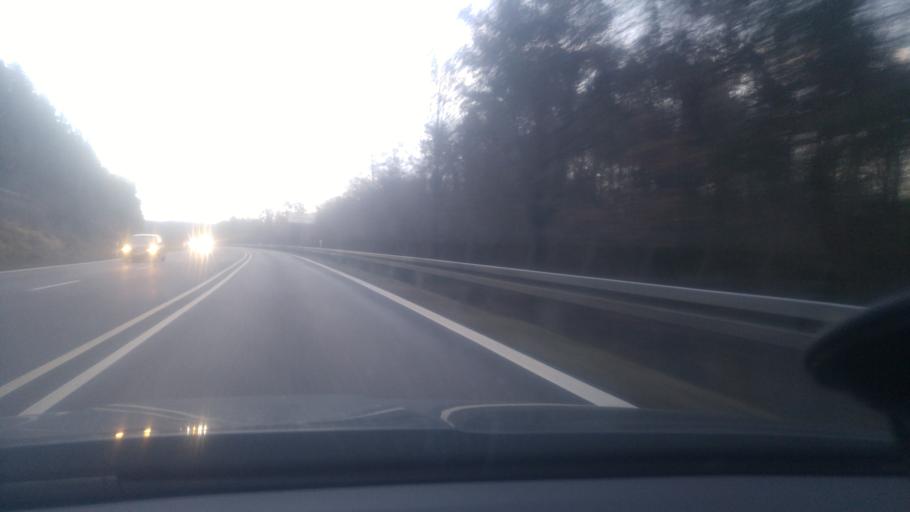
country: DE
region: Baden-Wuerttemberg
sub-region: Freiburg Region
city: Lauchringen
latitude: 47.6337
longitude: 8.3211
